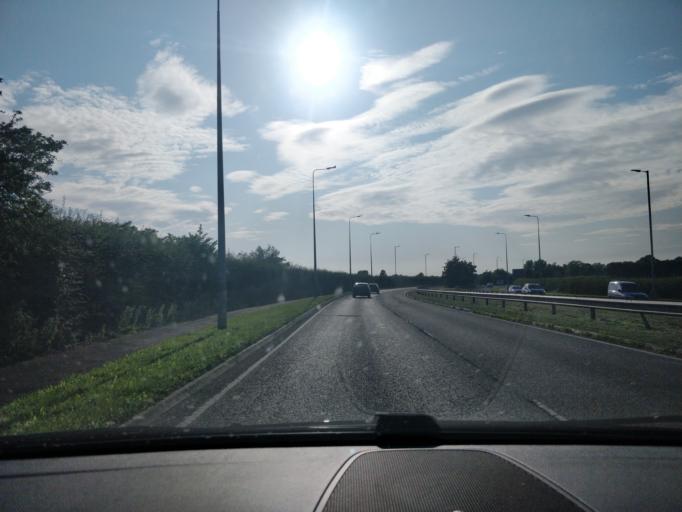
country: GB
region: England
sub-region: Lancashire
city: Banks
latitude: 53.6630
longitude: -2.8885
